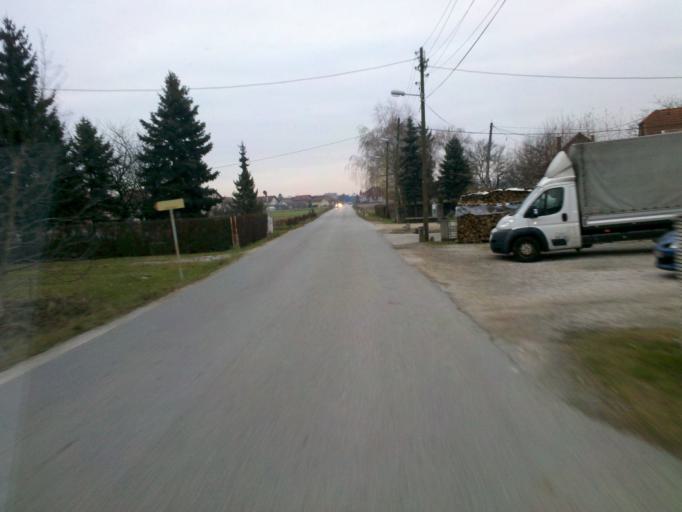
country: HR
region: Grad Zagreb
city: Lucko
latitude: 45.7585
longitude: 15.8711
